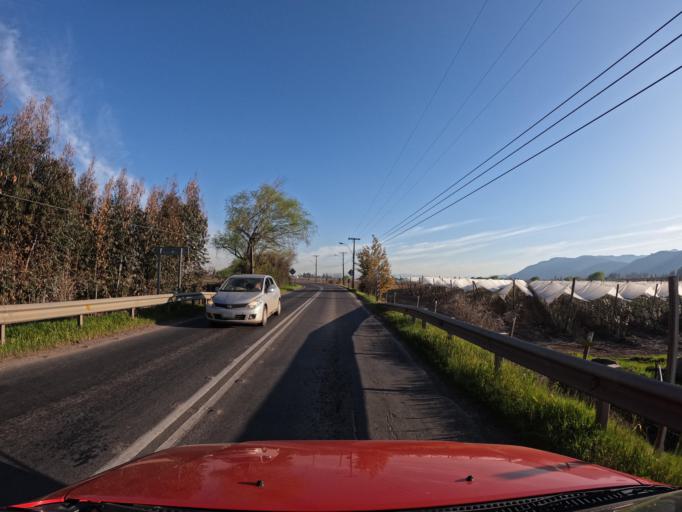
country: CL
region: Maule
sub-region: Provincia de Curico
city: Rauco
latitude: -34.8897
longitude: -71.2739
